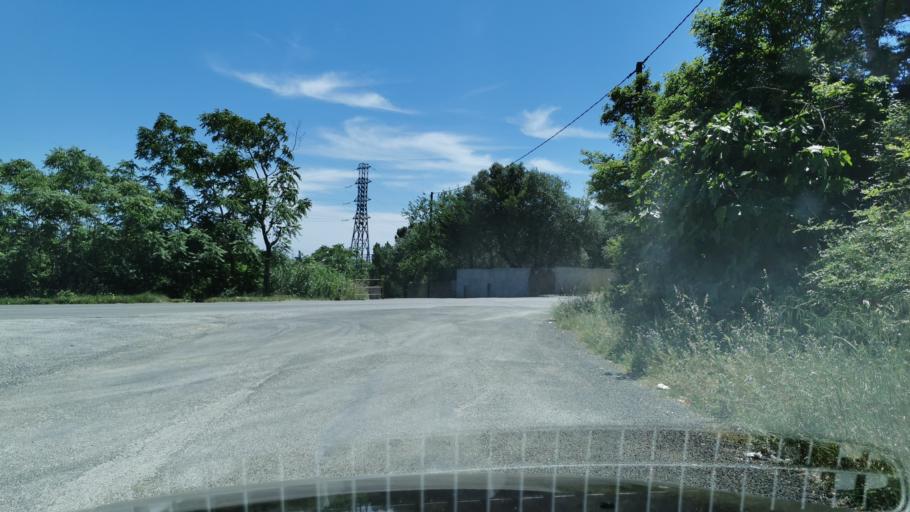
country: FR
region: Languedoc-Roussillon
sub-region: Departement de l'Aude
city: Narbonne
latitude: 43.1995
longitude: 2.9803
